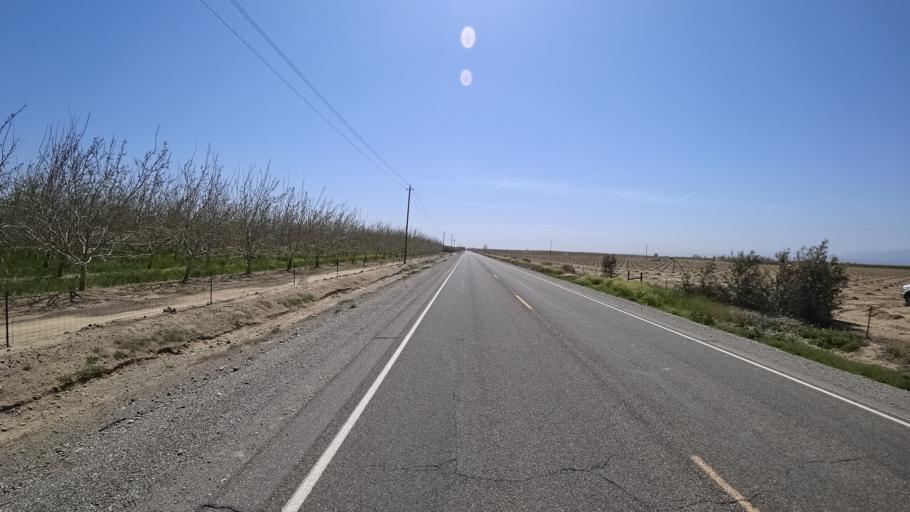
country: US
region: California
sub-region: Glenn County
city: Orland
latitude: 39.6557
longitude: -122.1971
